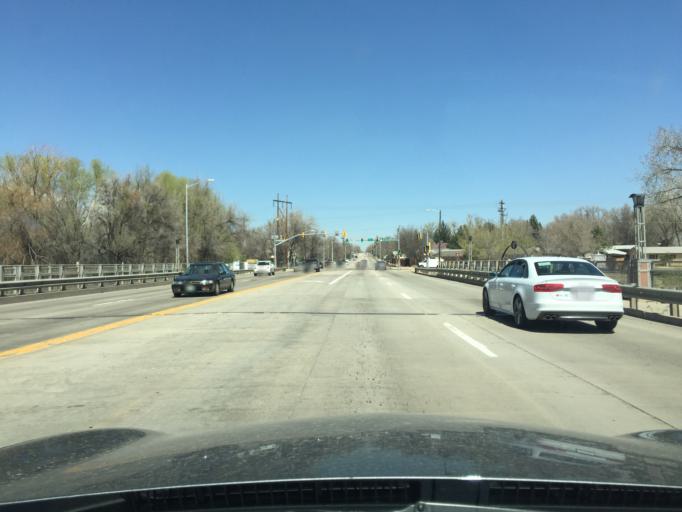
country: US
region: Colorado
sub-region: Boulder County
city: Longmont
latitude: 40.1659
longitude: -105.1308
